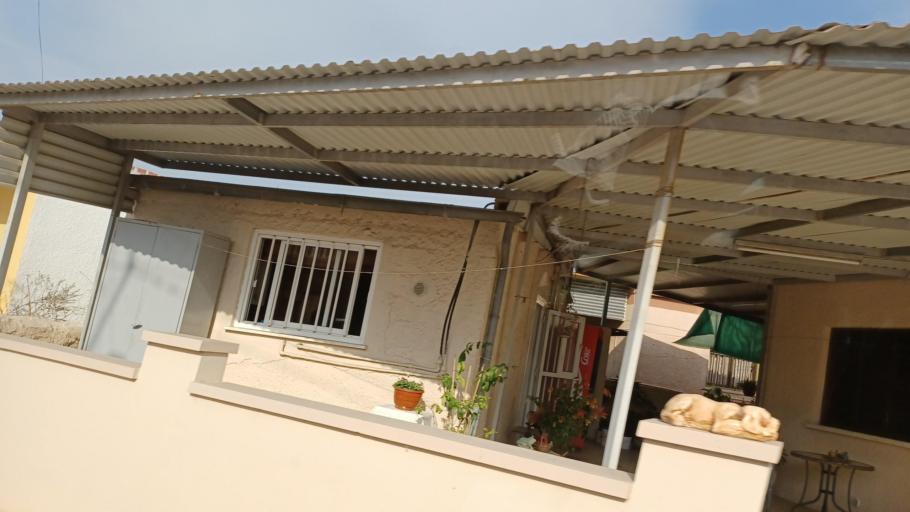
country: CY
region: Ammochostos
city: Frenaros
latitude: 35.0411
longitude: 33.9222
